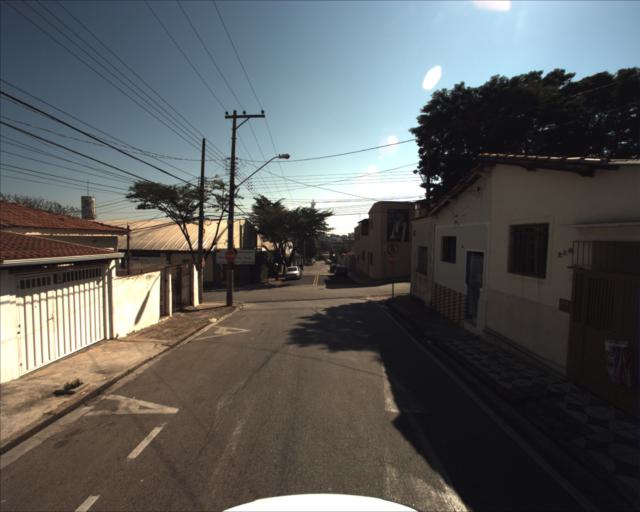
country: BR
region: Sao Paulo
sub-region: Sorocaba
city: Sorocaba
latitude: -23.4955
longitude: -47.4411
